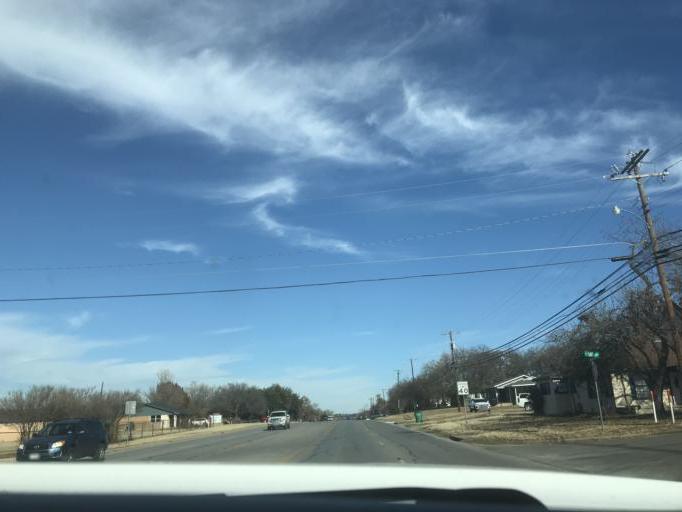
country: US
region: Texas
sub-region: Erath County
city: Stephenville
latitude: 32.2258
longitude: -98.2226
